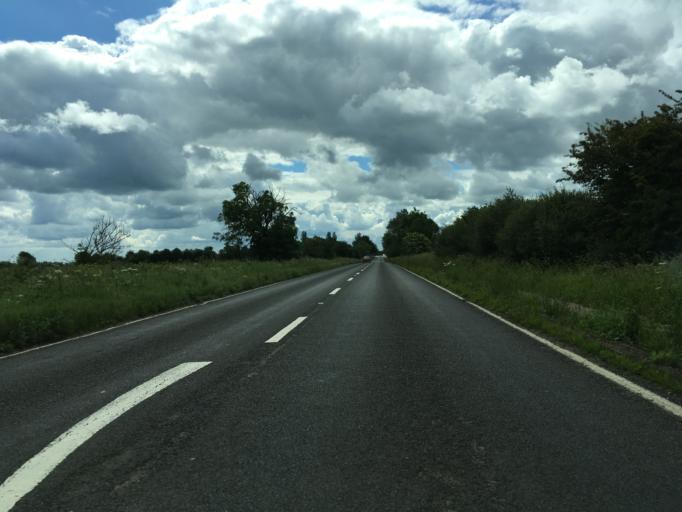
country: GB
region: England
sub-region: Oxfordshire
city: Chipping Norton
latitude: 51.9461
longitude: -1.5174
